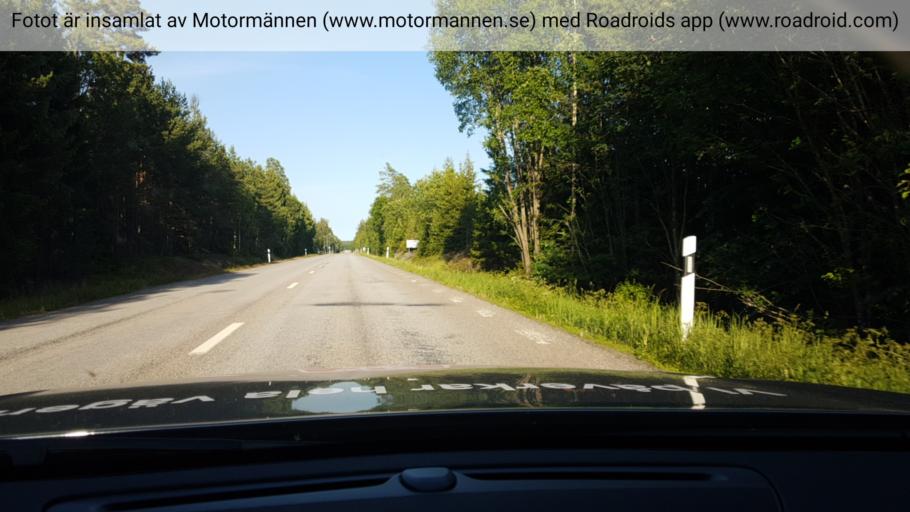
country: SE
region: Uppsala
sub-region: Osthammars Kommun
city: Gimo
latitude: 60.1651
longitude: 18.1624
